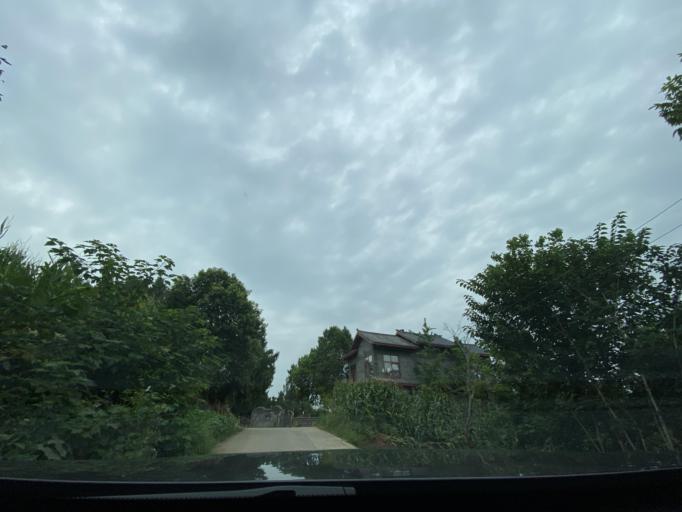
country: CN
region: Sichuan
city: Jiancheng
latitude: 30.3878
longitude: 104.4949
